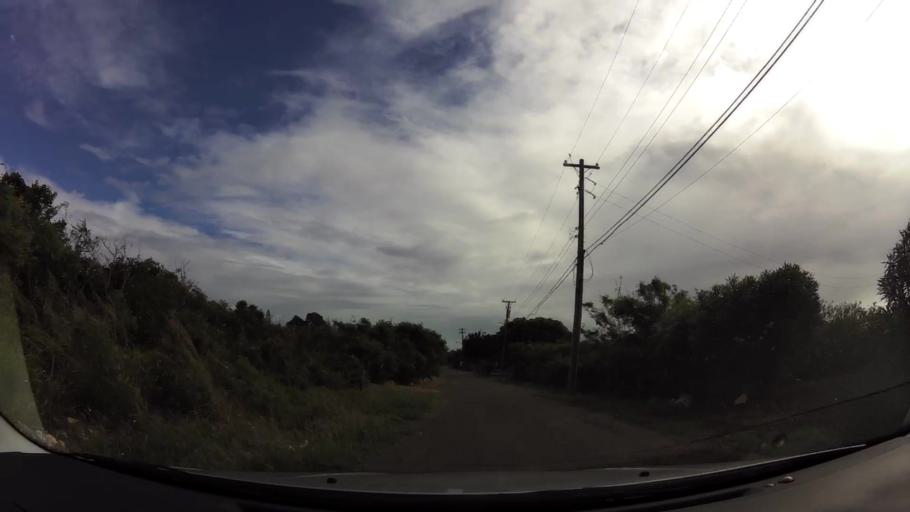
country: AG
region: Saint Peter
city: Parham
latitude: 17.1006
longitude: -61.6858
